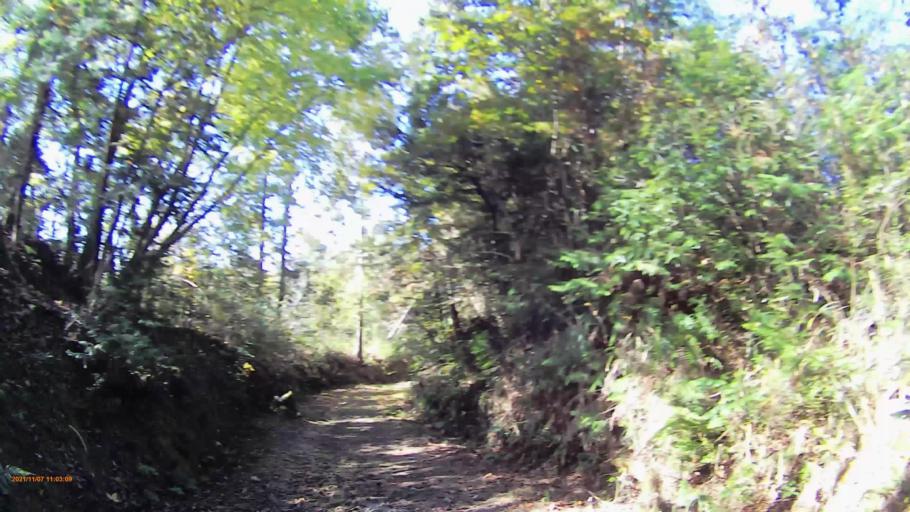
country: JP
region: Gifu
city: Mizunami
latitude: 35.4378
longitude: 137.3058
